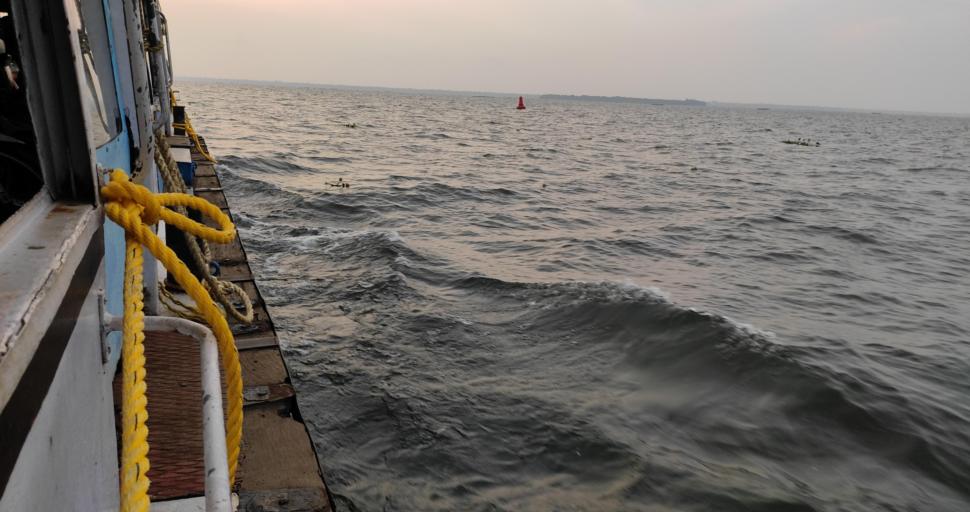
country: IN
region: Kerala
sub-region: Alappuzha
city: Shertallai
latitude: 9.6011
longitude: 76.4063
